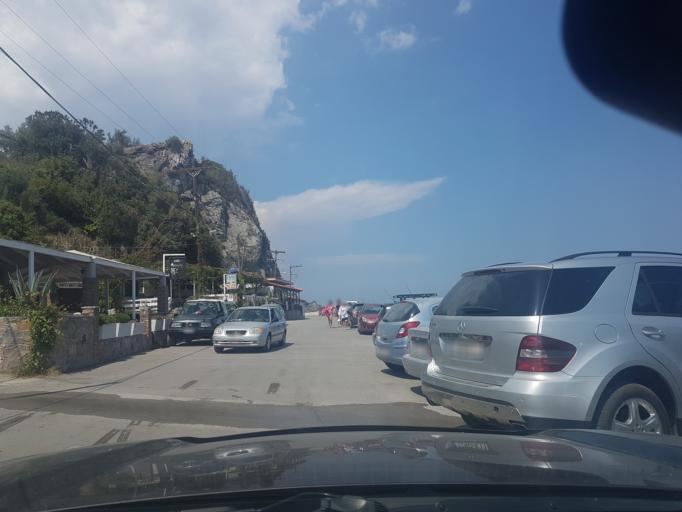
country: GR
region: Central Greece
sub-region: Nomos Evvoias
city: Kymi
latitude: 38.6689
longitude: 23.9248
